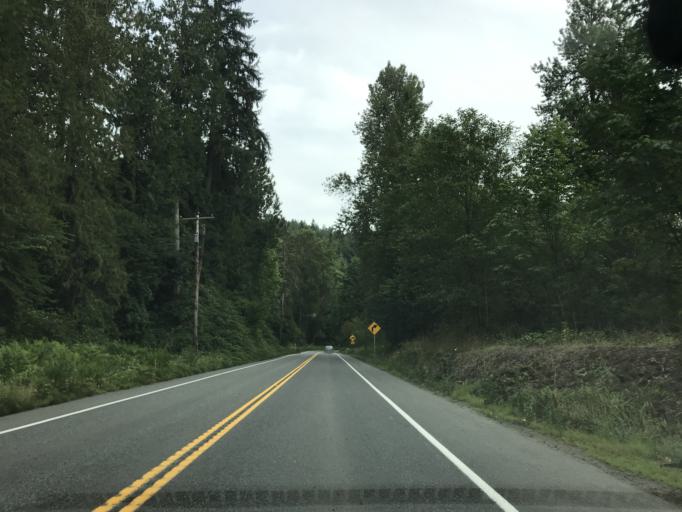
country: US
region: Washington
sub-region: King County
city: Fall City
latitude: 47.5503
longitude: -121.8995
